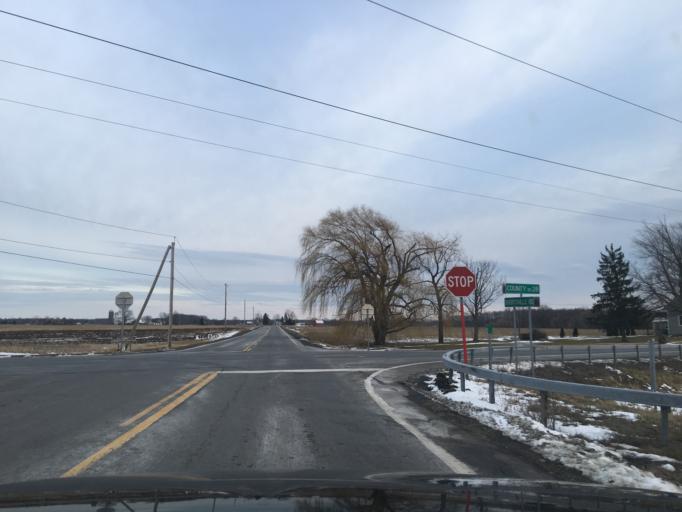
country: US
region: New York
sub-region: Ontario County
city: Manchester
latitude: 42.9561
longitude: -77.2772
